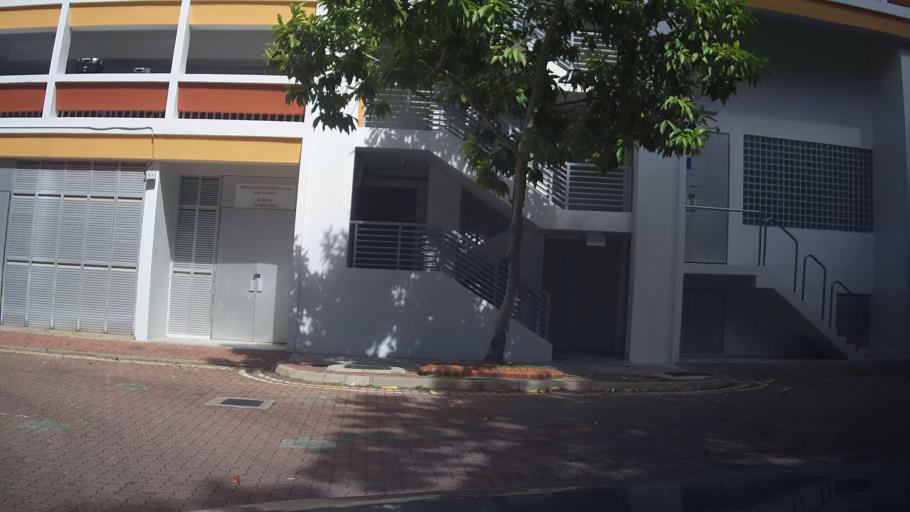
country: SG
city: Singapore
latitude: 1.3627
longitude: 103.9602
